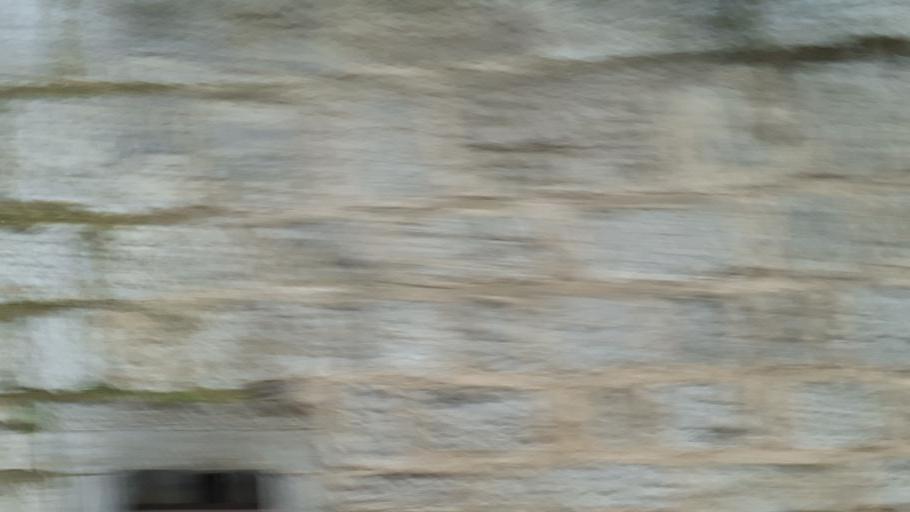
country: FR
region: Franche-Comte
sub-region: Departement du Doubs
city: Novillars
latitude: 47.2840
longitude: 6.1521
